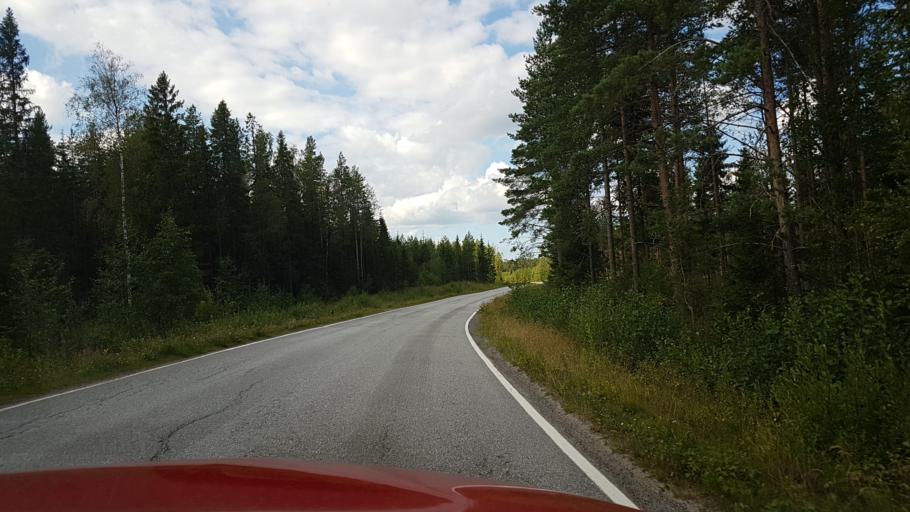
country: FI
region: Northern Ostrobothnia
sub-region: Ylivieska
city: Himanka
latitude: 64.0764
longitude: 23.7116
